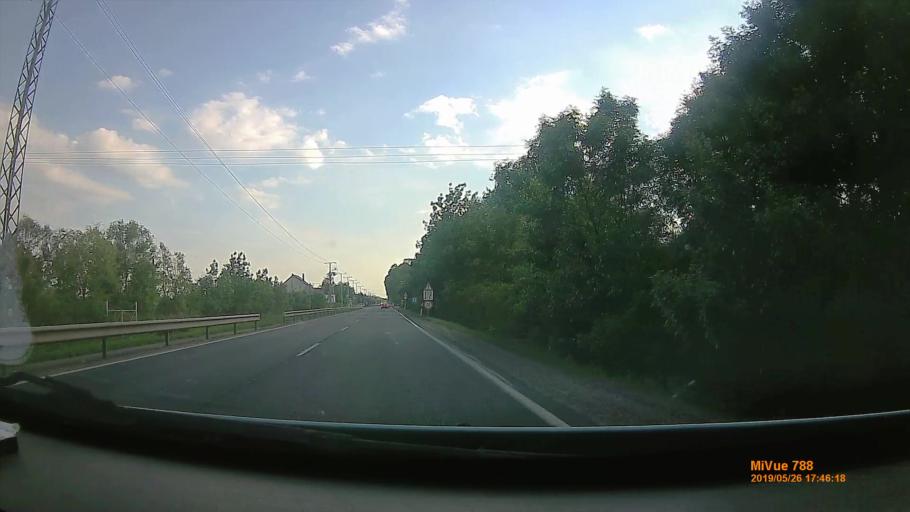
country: HU
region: Borsod-Abauj-Zemplen
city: Szikszo
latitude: 48.2095
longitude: 20.9396
